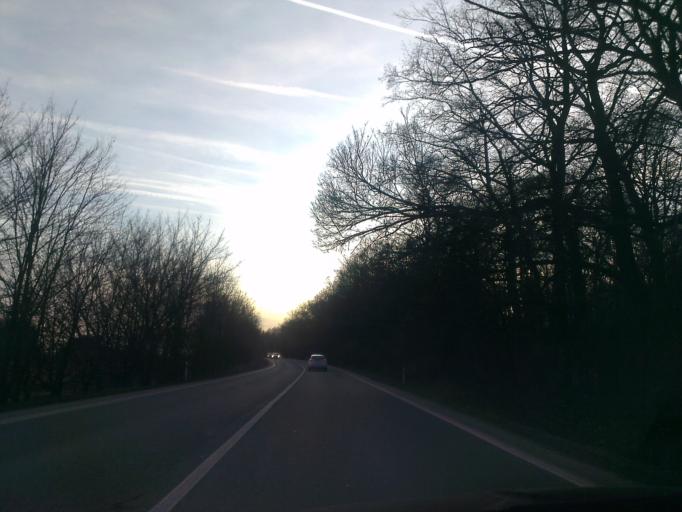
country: CZ
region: South Moravian
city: Bilovice nad Svitavou
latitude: 49.2229
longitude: 16.6848
